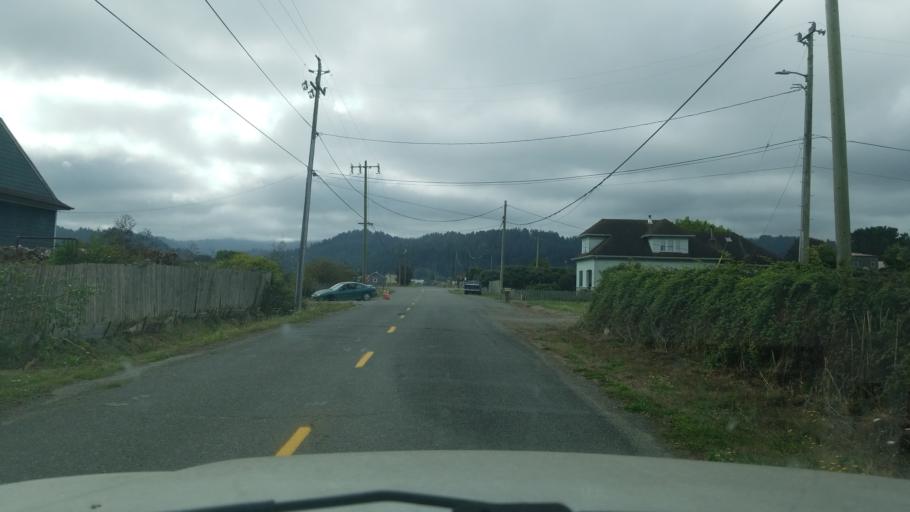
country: US
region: California
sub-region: Humboldt County
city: Ferndale
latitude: 40.5904
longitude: -124.2552
